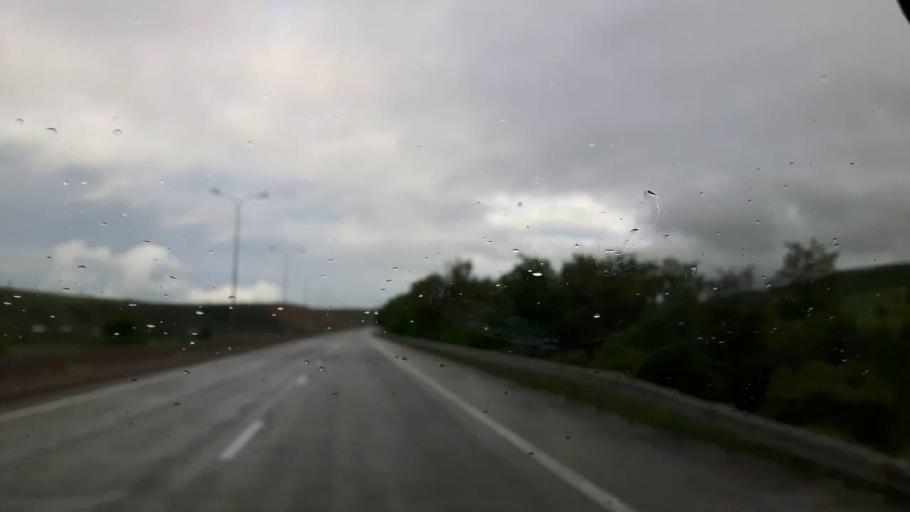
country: GE
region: Shida Kartli
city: Kaspi
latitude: 42.0011
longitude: 44.3823
